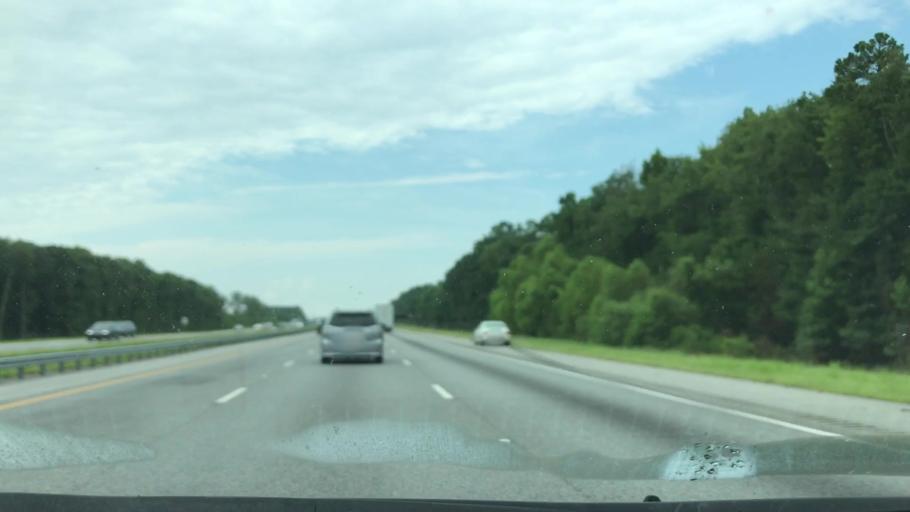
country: US
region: Georgia
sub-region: McIntosh County
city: Darien
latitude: 31.4909
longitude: -81.4471
